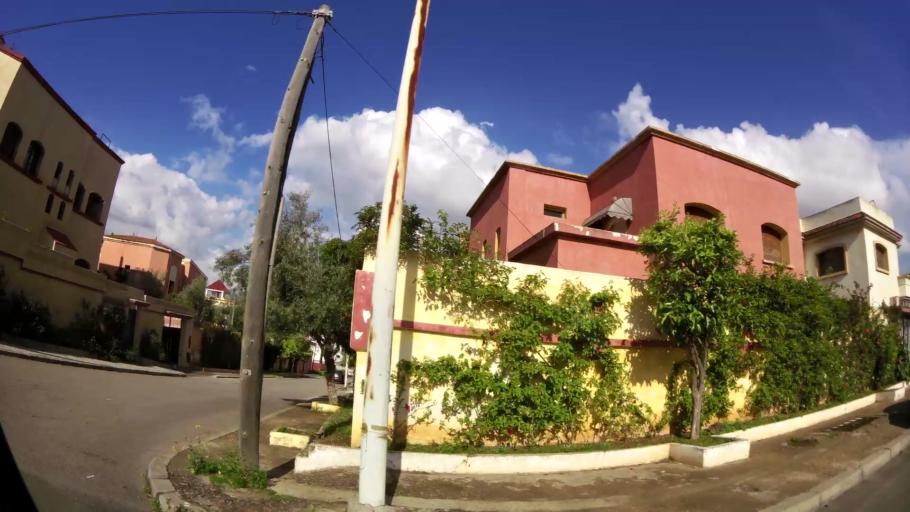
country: MA
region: Chaouia-Ouardigha
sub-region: Settat Province
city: Settat
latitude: 33.0100
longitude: -7.6288
